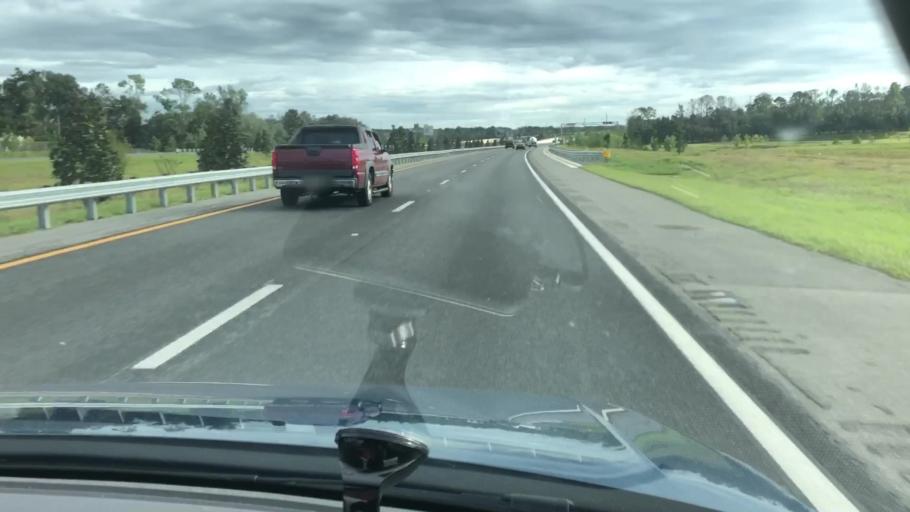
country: US
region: Florida
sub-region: Orange County
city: Zellwood
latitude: 28.7371
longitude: -81.5648
